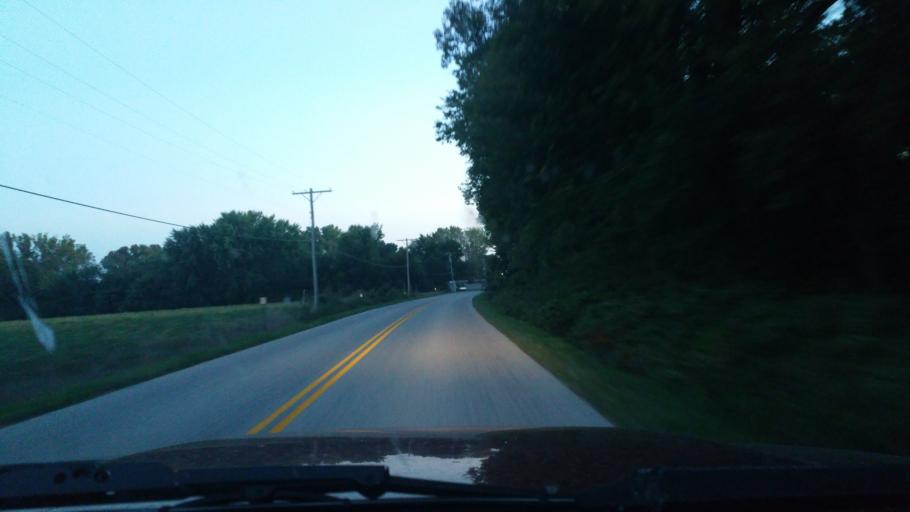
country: US
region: Kansas
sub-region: Riley County
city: Manhattan
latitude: 39.2493
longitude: -96.5701
